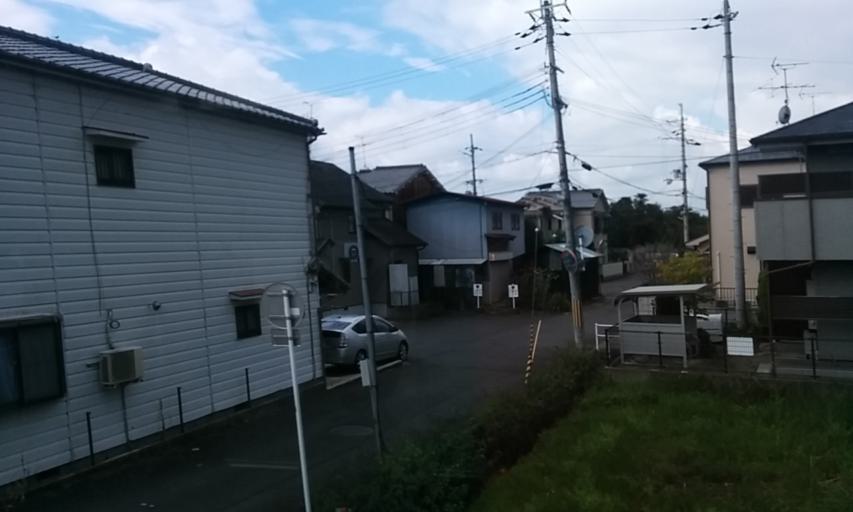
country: JP
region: Nara
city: Tawaramoto
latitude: 34.5456
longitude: 135.7932
